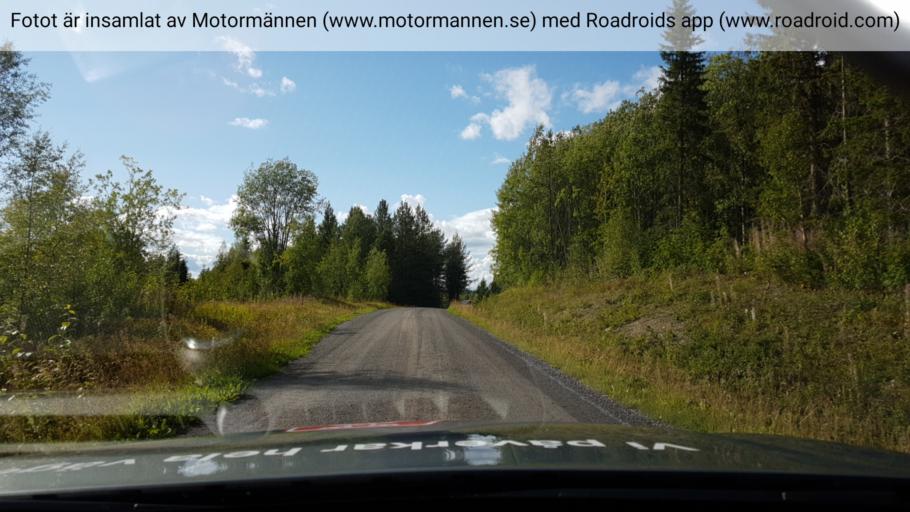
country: SE
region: Jaemtland
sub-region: OEstersunds Kommun
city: Lit
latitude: 63.3258
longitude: 15.1913
